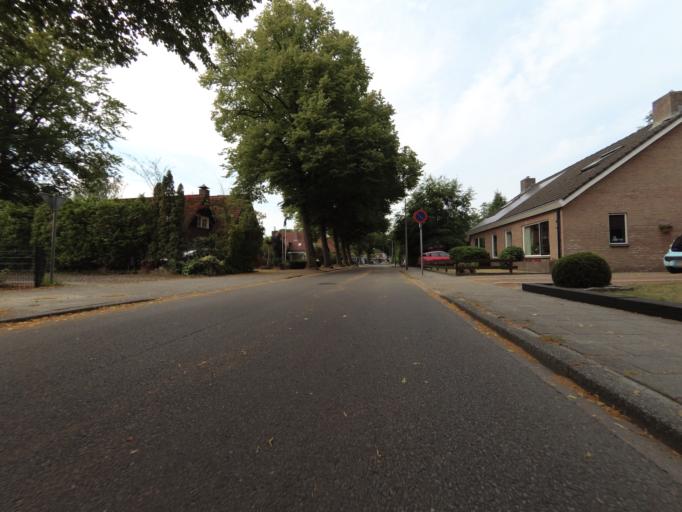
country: NL
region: Overijssel
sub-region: Gemeente Hengelo
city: Hengelo
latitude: 52.2054
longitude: 6.8002
